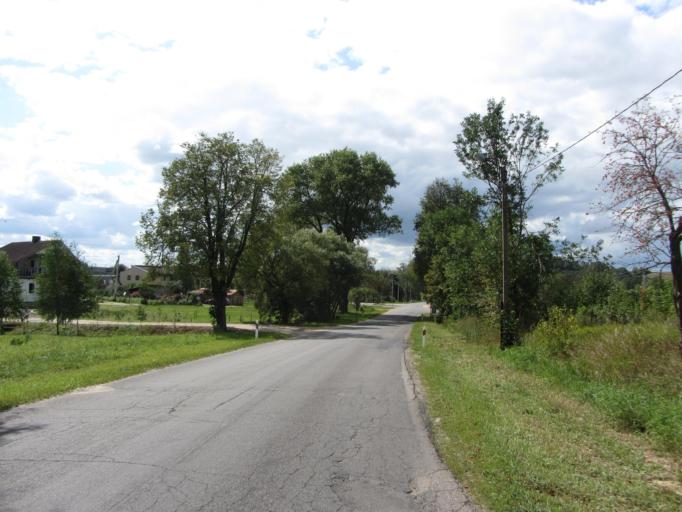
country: LT
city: Baltoji Voke
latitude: 54.6174
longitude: 25.1398
